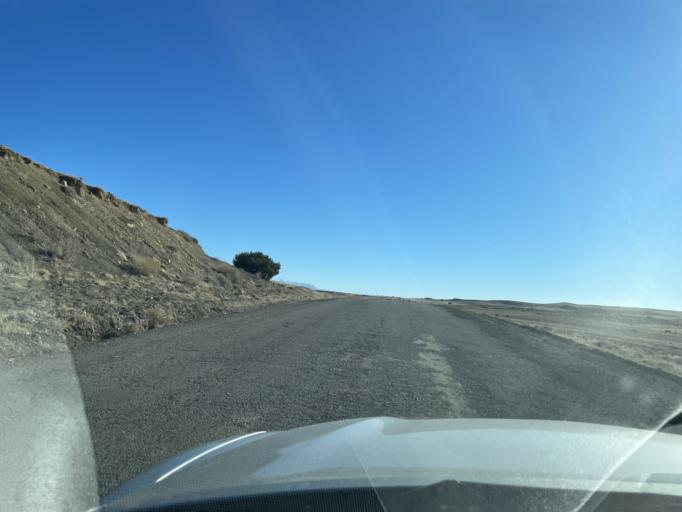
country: US
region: Colorado
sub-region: Mesa County
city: Loma
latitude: 39.1971
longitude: -109.1223
